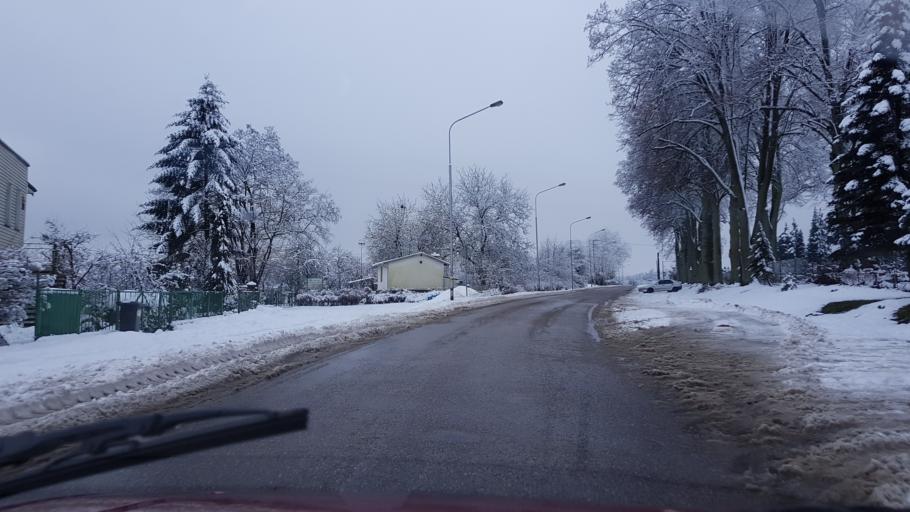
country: PL
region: West Pomeranian Voivodeship
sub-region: Powiat drawski
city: Zlocieniec
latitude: 53.5271
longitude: 16.0091
